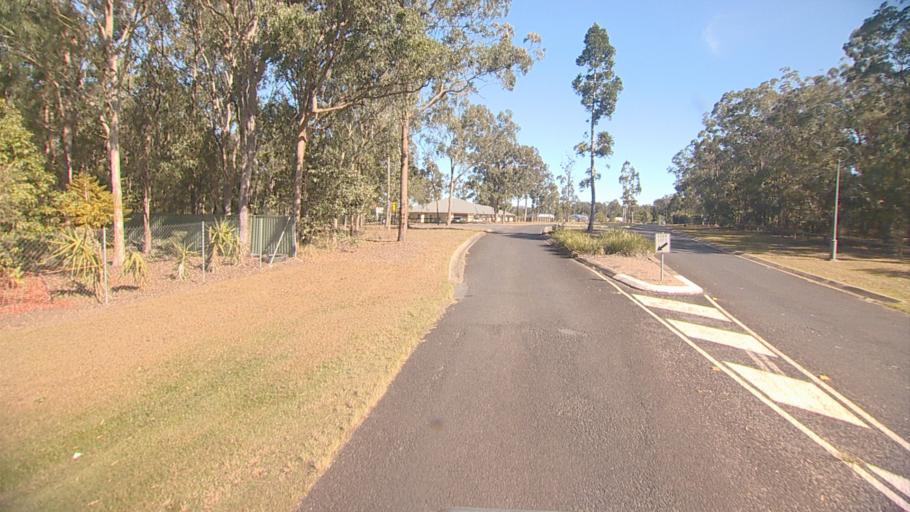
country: AU
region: Queensland
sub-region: Ipswich
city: Springfield Lakes
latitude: -27.7338
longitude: 152.9229
